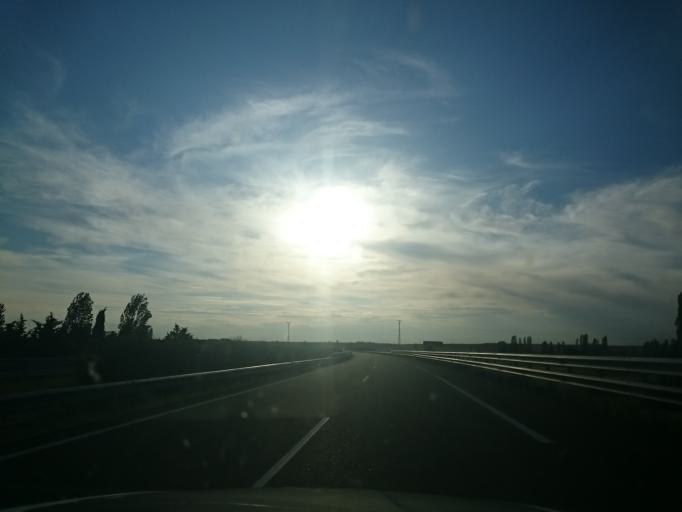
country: ES
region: Castille and Leon
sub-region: Provincia de Leon
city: Sahagun
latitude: 42.3740
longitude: -4.9944
